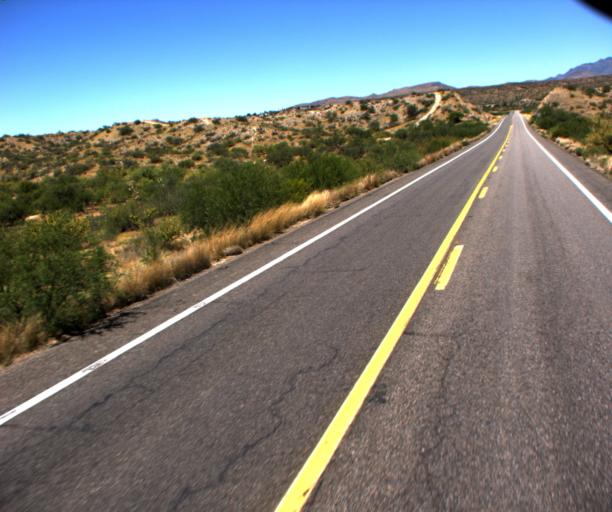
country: US
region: Arizona
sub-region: Gila County
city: Globe
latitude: 33.3652
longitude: -110.7369
